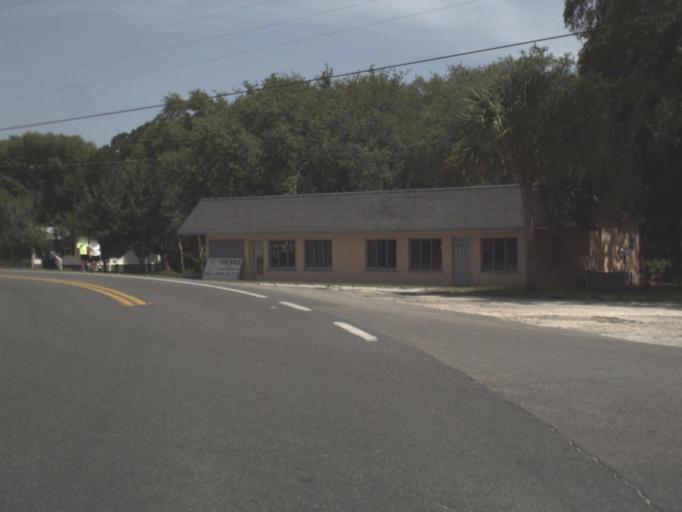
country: US
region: Florida
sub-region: Taylor County
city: Steinhatchee
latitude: 29.6726
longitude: -83.3895
